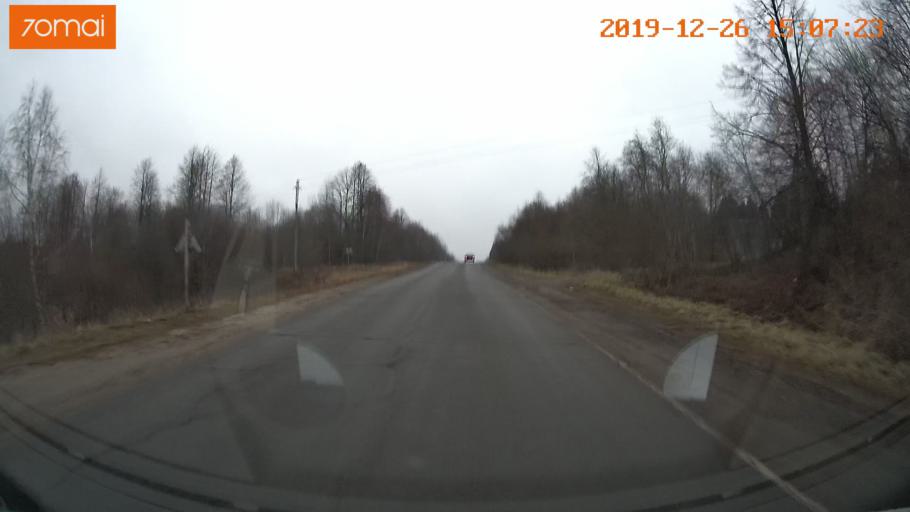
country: RU
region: Jaroslavl
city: Rybinsk
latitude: 58.1703
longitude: 38.8409
